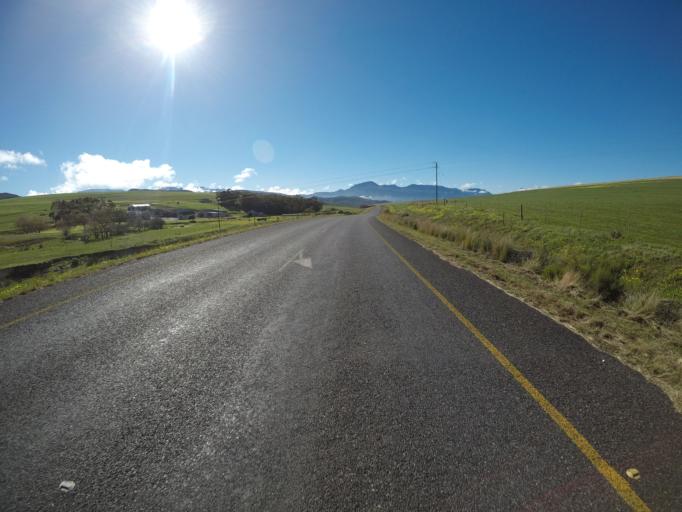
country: ZA
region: Western Cape
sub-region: Overberg District Municipality
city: Caledon
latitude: -34.1247
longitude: 19.5146
